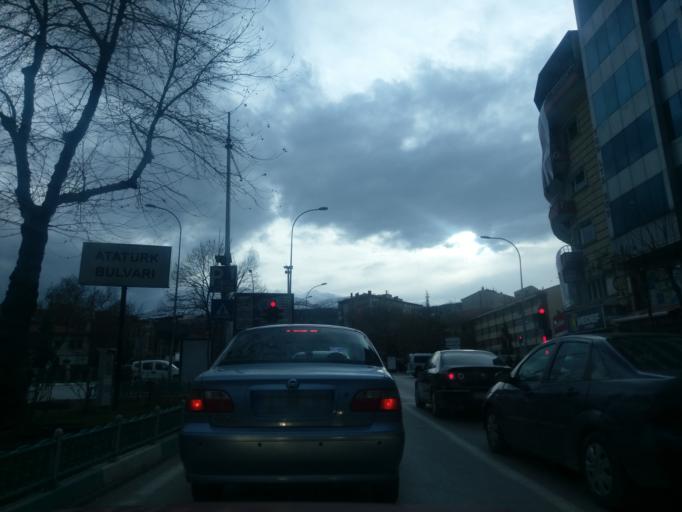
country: TR
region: Kuetahya
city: Kutahya
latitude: 39.4204
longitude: 29.9859
